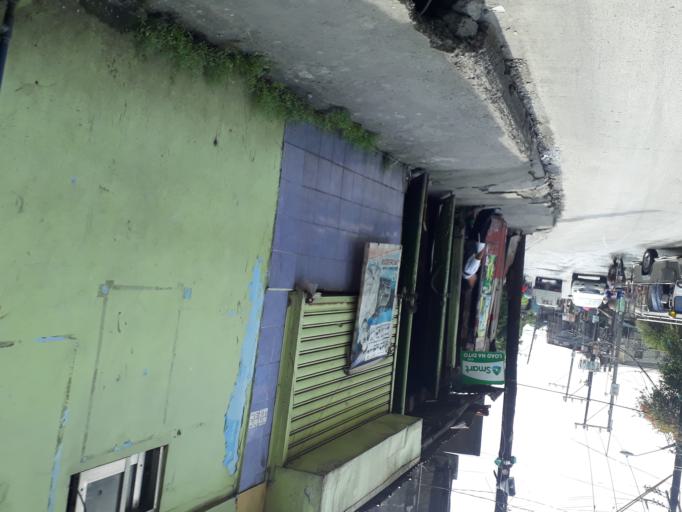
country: PH
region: Calabarzon
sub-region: Province of Rizal
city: Valenzuela
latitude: 14.7051
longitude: 121.0086
